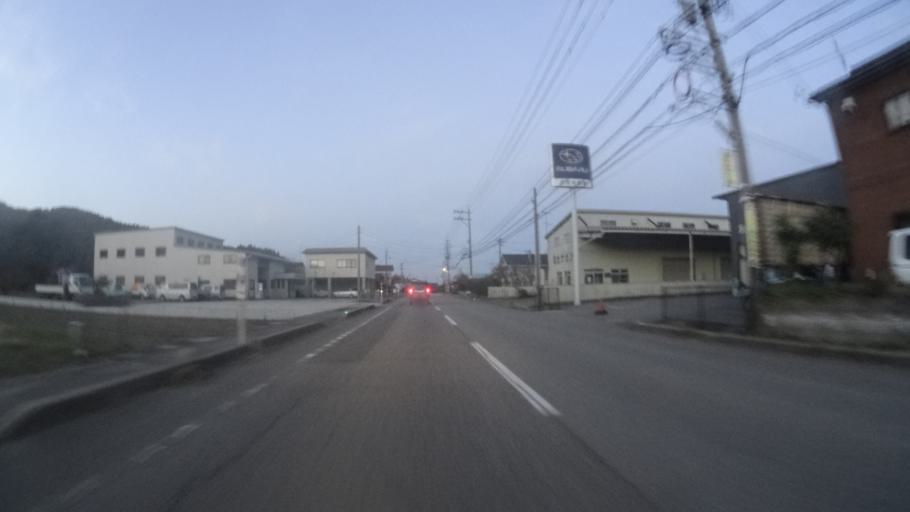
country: JP
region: Ishikawa
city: Nanao
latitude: 37.3811
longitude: 136.8864
